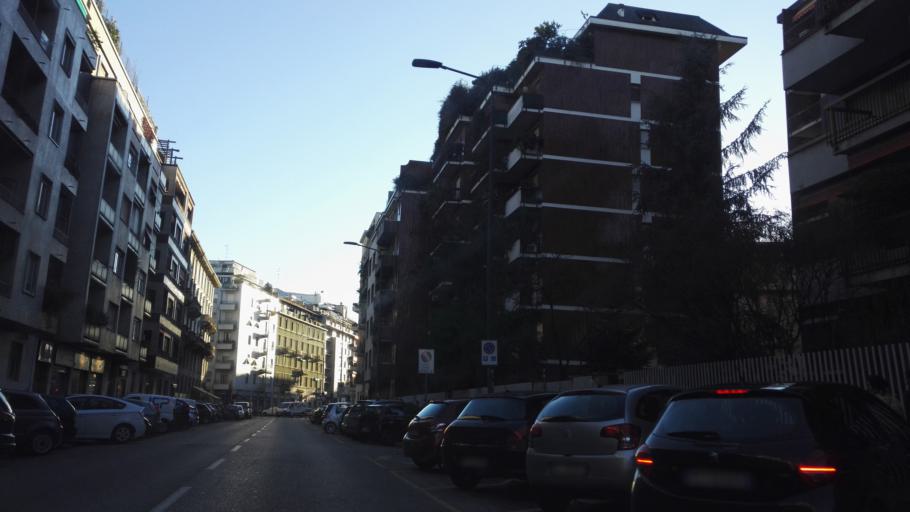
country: IT
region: Lombardy
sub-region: Citta metropolitana di Milano
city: Milano
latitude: 45.4595
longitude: 9.2110
